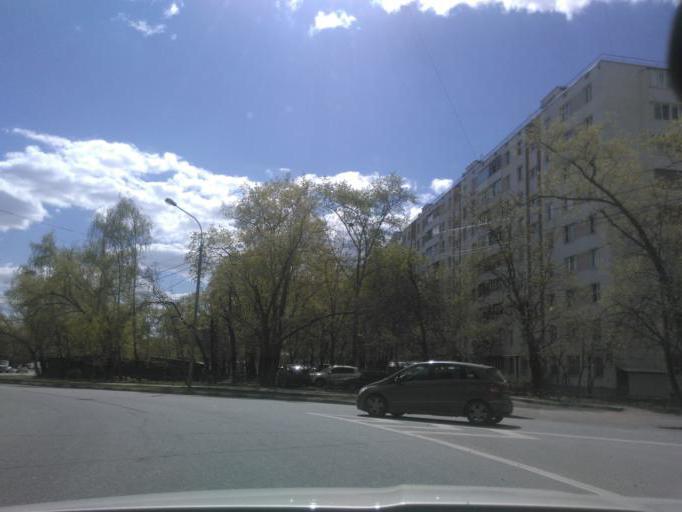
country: RU
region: Moscow
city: Novokhovrino
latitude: 55.8622
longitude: 37.5045
